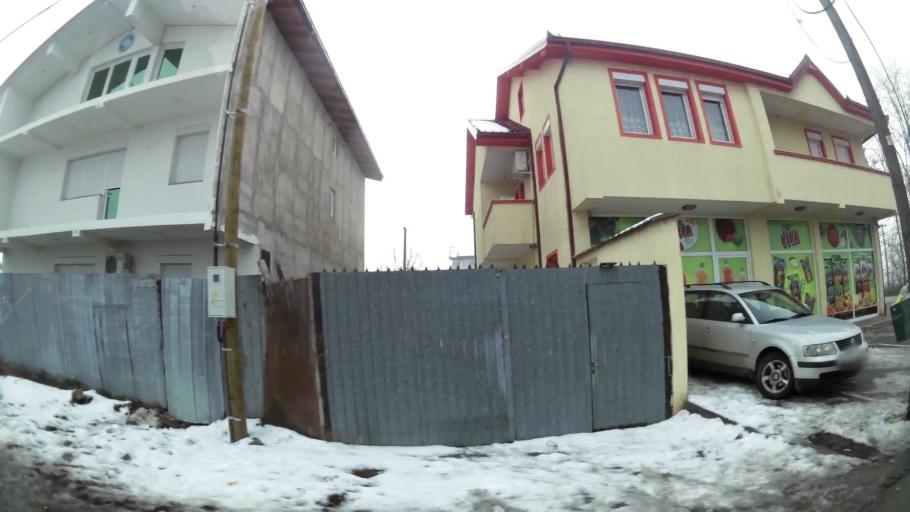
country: MK
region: Ilinden
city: Idrizovo
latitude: 41.9571
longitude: 21.5715
